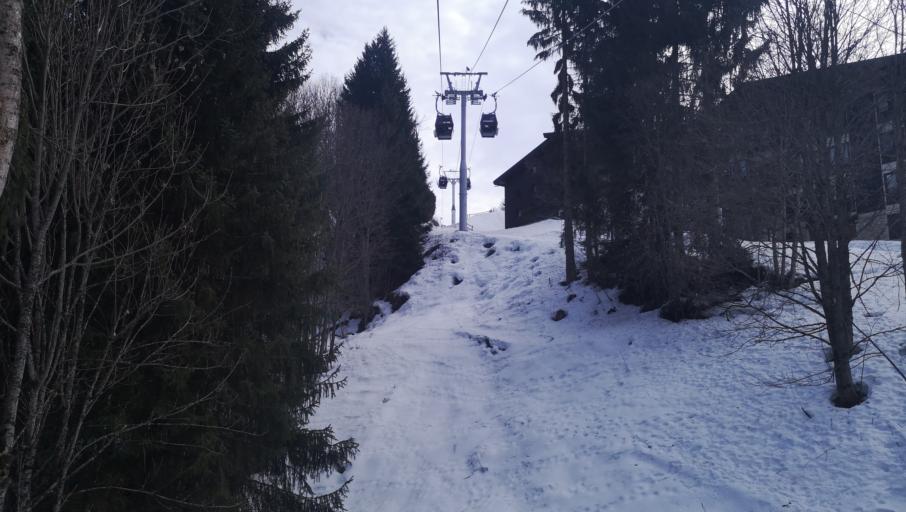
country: FR
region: Rhone-Alpes
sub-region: Departement de la Haute-Savoie
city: Megeve
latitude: 45.8505
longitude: 6.6217
